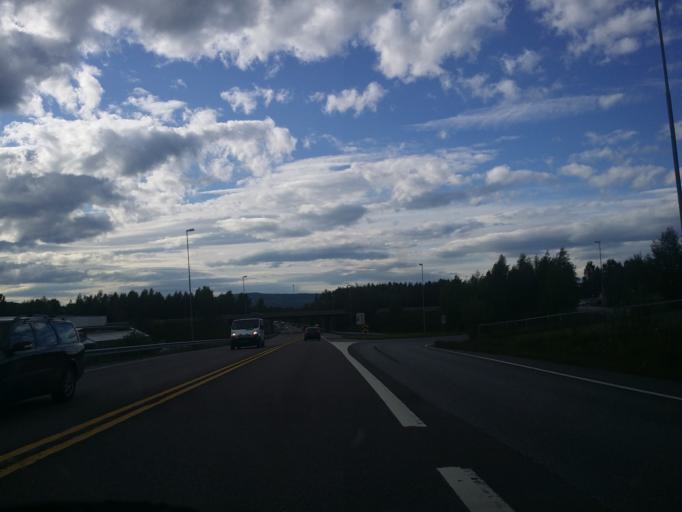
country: NO
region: Hedmark
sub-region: Hamar
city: Hamar
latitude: 60.7984
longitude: 11.1193
